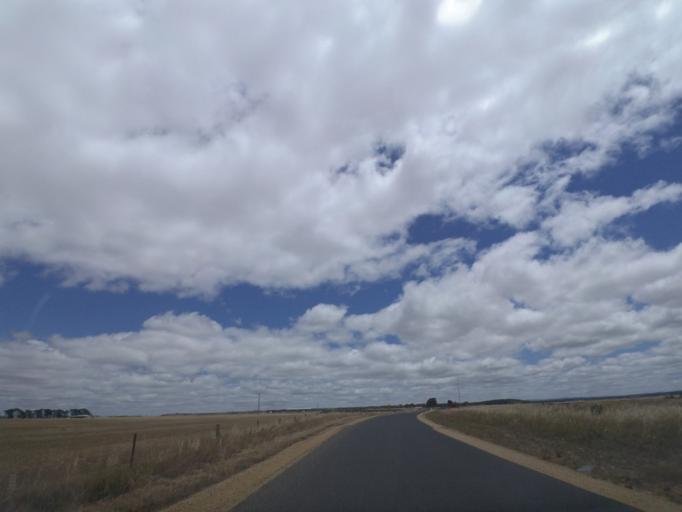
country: AU
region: Victoria
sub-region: Moorabool
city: Bacchus Marsh
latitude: -37.6827
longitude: 144.3559
